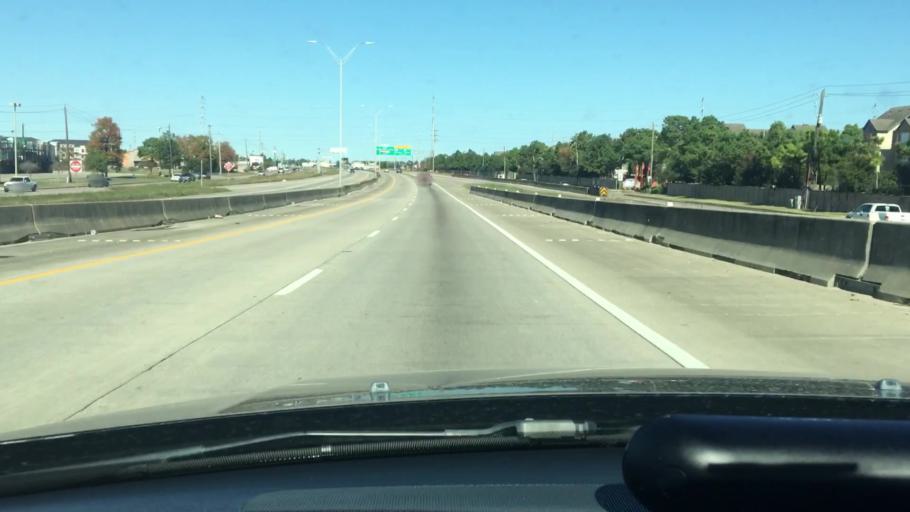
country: US
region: Texas
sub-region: Harris County
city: Cloverleaf
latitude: 29.8117
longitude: -95.1635
